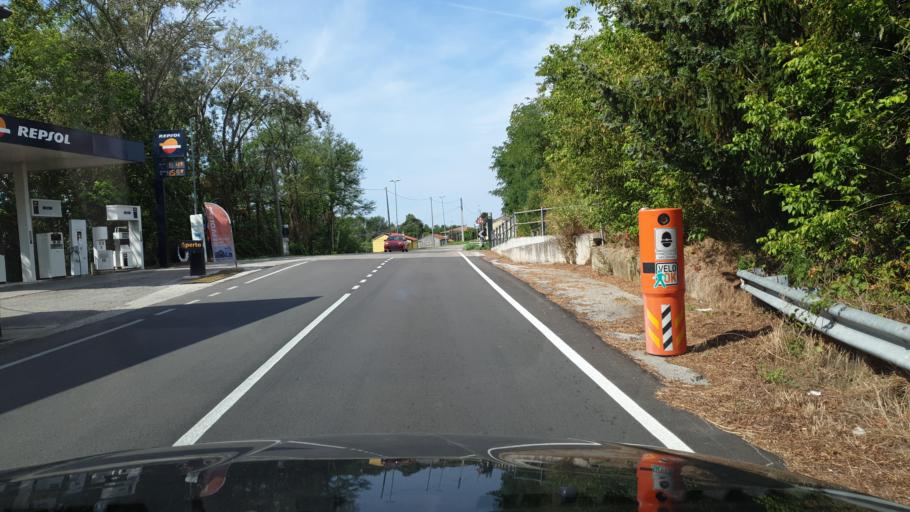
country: IT
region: Veneto
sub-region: Provincia di Rovigo
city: Pincara
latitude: 45.0012
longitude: 11.6227
